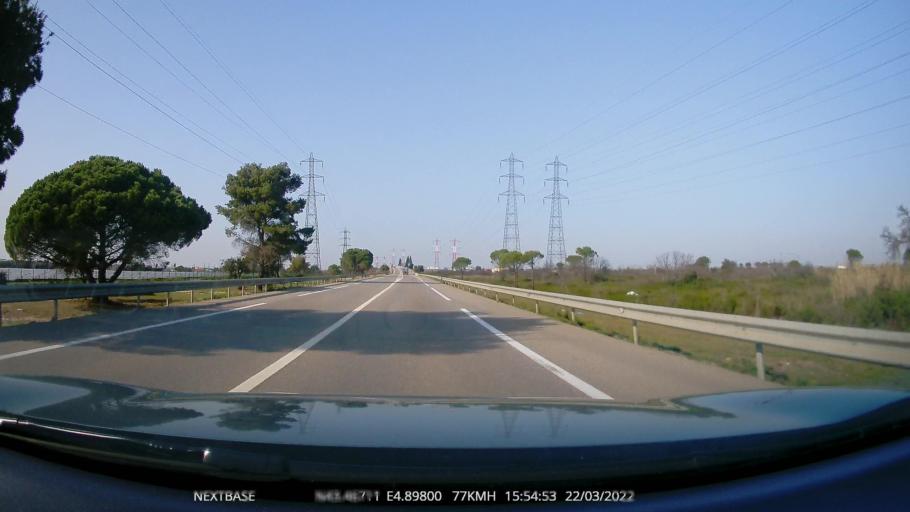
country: FR
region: Provence-Alpes-Cote d'Azur
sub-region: Departement des Bouches-du-Rhone
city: Fos-sur-Mer
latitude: 43.4667
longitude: 4.8981
